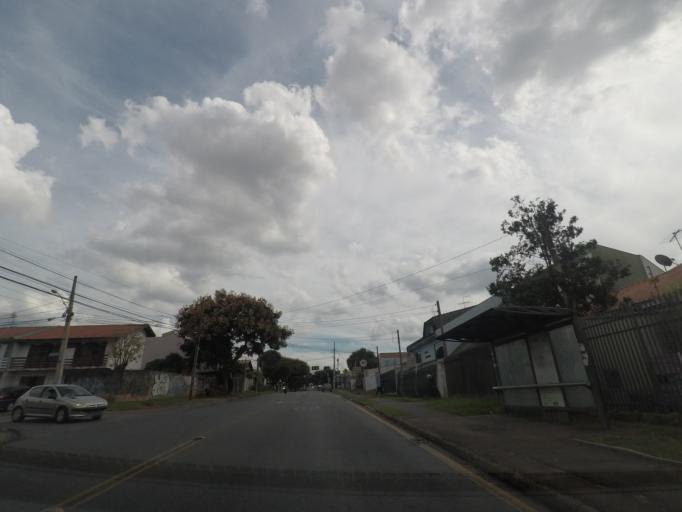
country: BR
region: Parana
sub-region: Sao Jose Dos Pinhais
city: Sao Jose dos Pinhais
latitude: -25.4924
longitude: -49.2595
